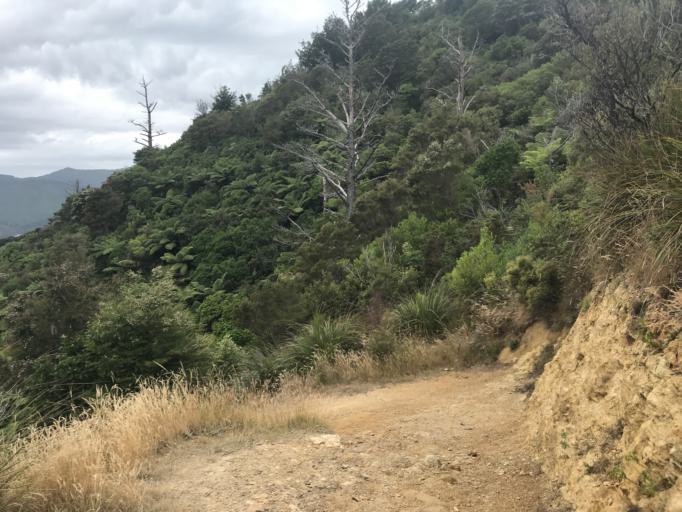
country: NZ
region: Marlborough
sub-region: Marlborough District
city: Picton
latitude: -41.2183
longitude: 173.9755
